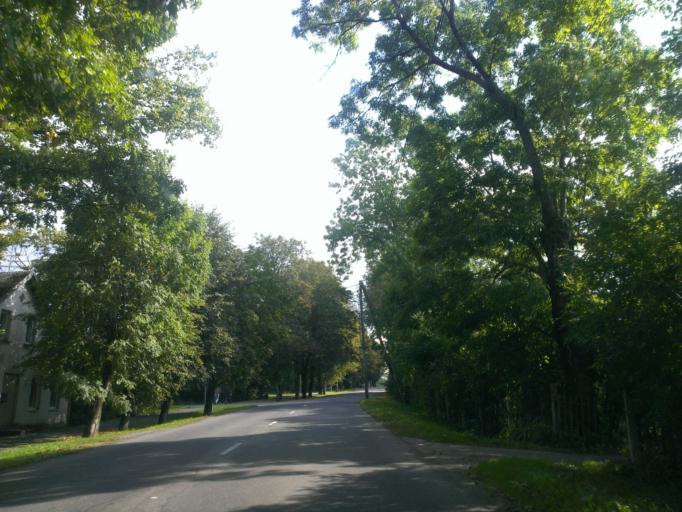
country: LV
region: Sigulda
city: Sigulda
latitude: 57.1507
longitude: 24.8538
